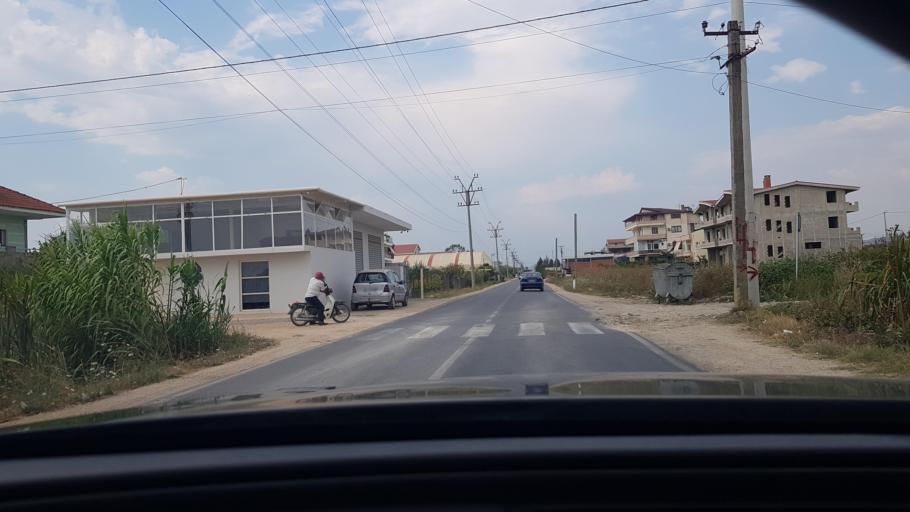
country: AL
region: Durres
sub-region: Rrethi i Durresit
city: Sukth
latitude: 41.4045
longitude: 19.5467
